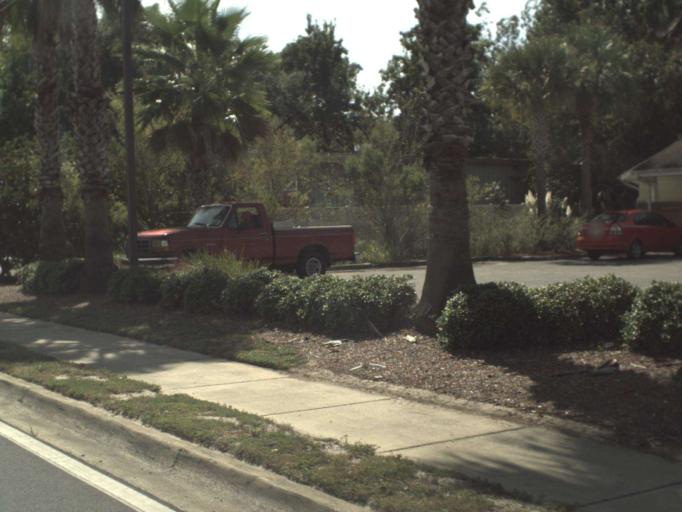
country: US
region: Florida
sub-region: Bay County
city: Lynn Haven
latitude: 30.2435
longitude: -85.6488
